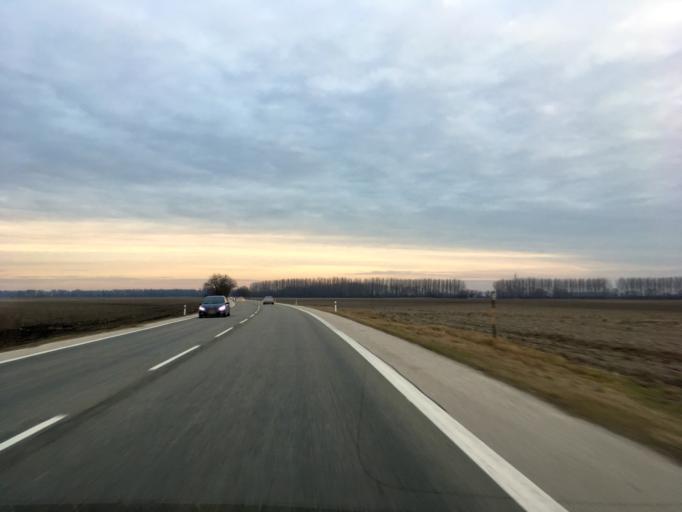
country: SK
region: Trnavsky
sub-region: Okres Dunajska Streda
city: Velky Meder
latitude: 47.9155
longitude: 17.7284
